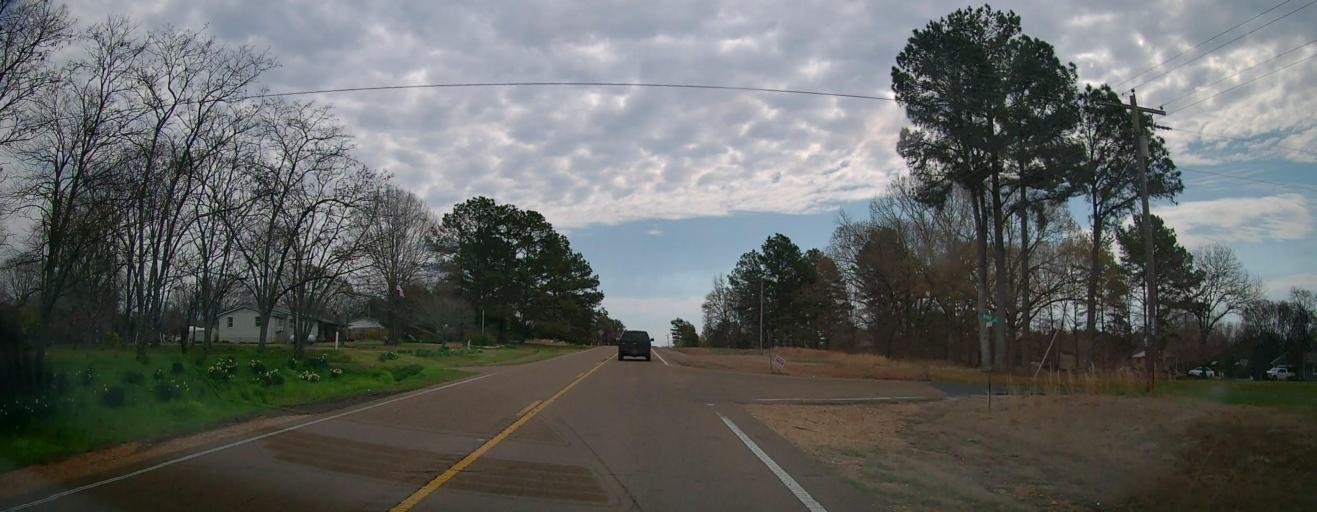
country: US
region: Mississippi
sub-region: Marshall County
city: Byhalia
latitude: 34.8411
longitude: -89.6029
